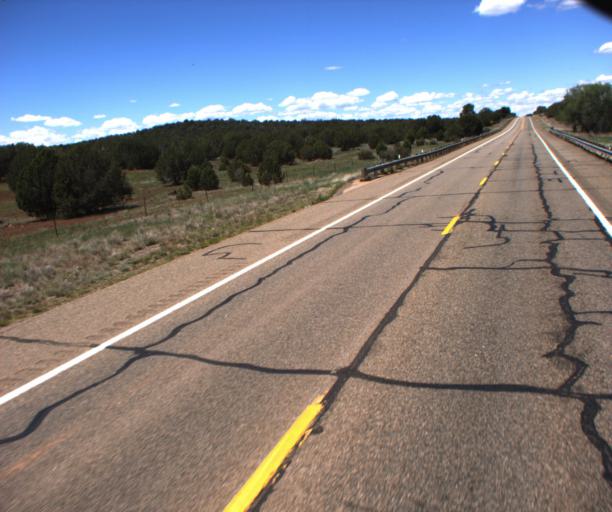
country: US
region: Arizona
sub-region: Yavapai County
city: Paulden
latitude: 35.1284
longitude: -112.4374
